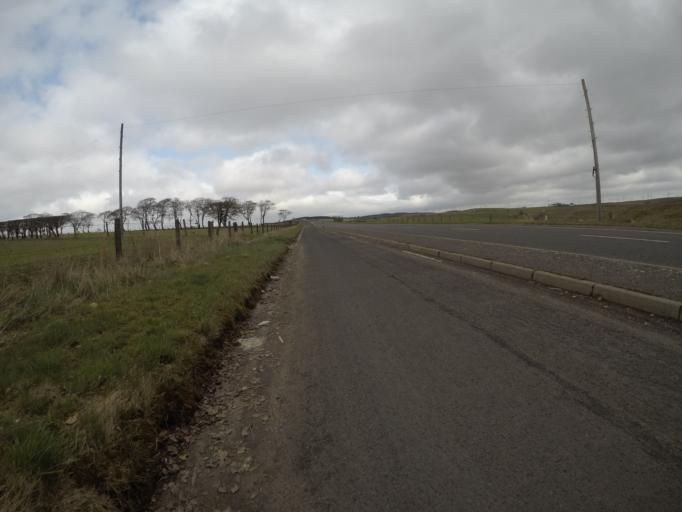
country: GB
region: Scotland
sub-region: East Ayrshire
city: Galston
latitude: 55.6870
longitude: -4.4140
